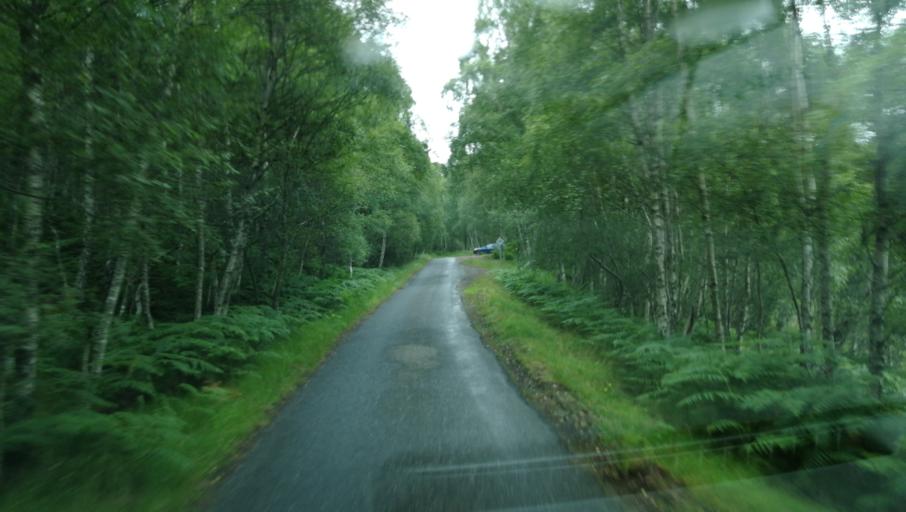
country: GB
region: Scotland
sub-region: Highland
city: Spean Bridge
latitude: 57.2827
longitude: -4.9297
